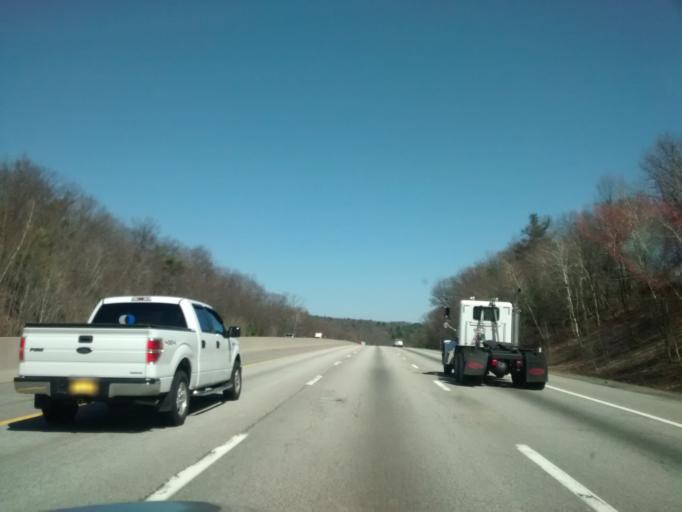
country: US
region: Massachusetts
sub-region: Worcester County
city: Grafton
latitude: 42.2275
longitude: -71.6639
